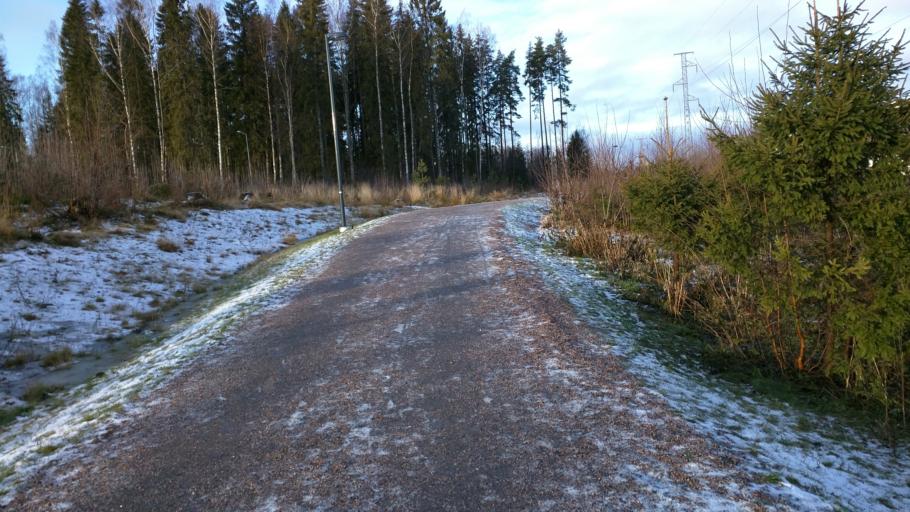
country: FI
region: Uusimaa
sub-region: Helsinki
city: Kilo
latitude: 60.2562
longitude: 24.7975
